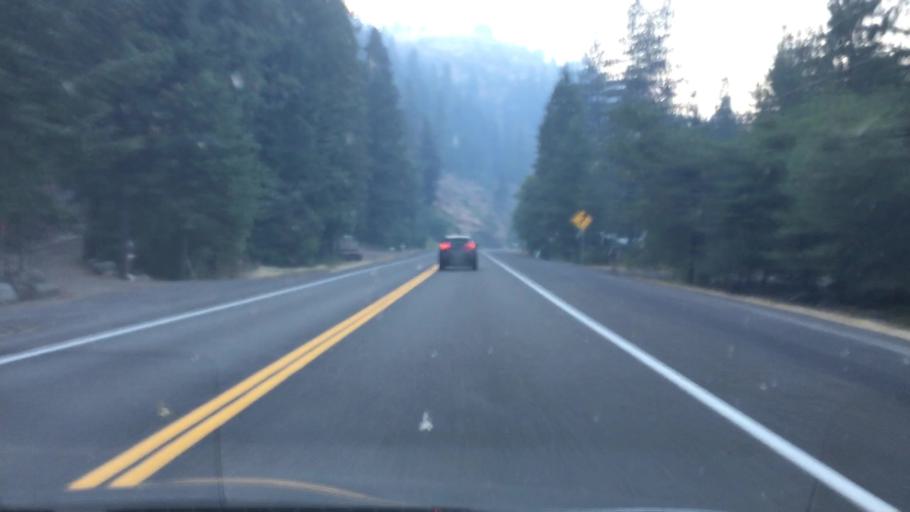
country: US
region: Idaho
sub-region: Valley County
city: McCall
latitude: 45.2285
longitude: -116.3236
